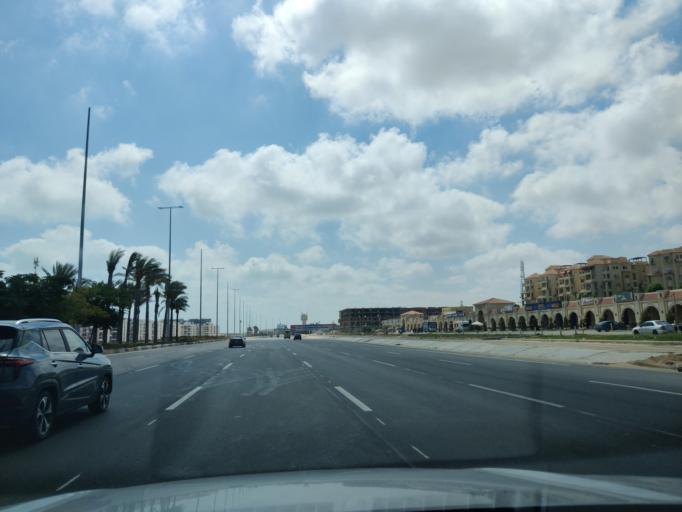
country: EG
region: Muhafazat Matruh
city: Al `Alamayn
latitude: 30.8456
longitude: 28.9350
